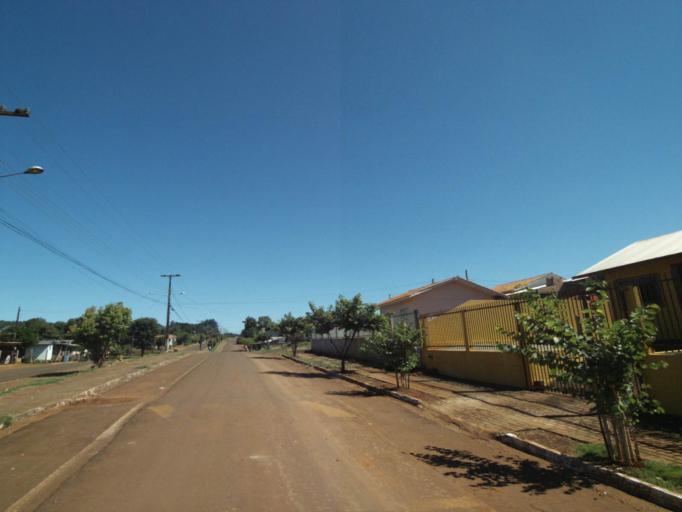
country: BR
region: Santa Catarina
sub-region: Sao Lourenco Do Oeste
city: Sao Lourenco dOeste
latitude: -26.2729
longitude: -52.7803
